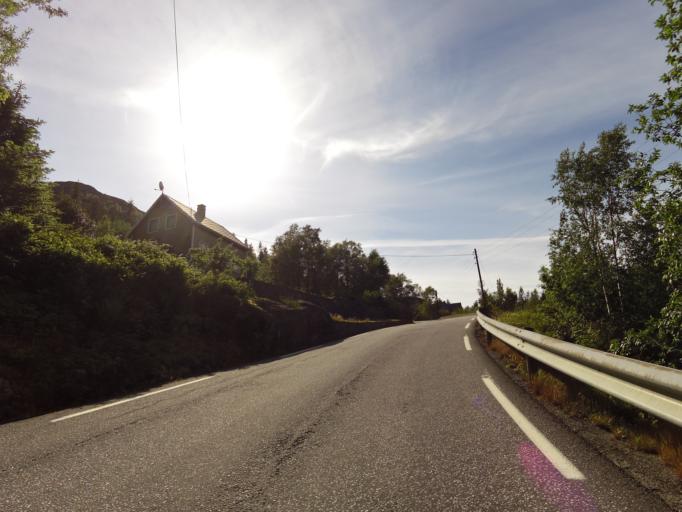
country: NO
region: Rogaland
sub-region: Sokndal
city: Hauge i Dalane
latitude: 58.3149
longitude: 6.3446
